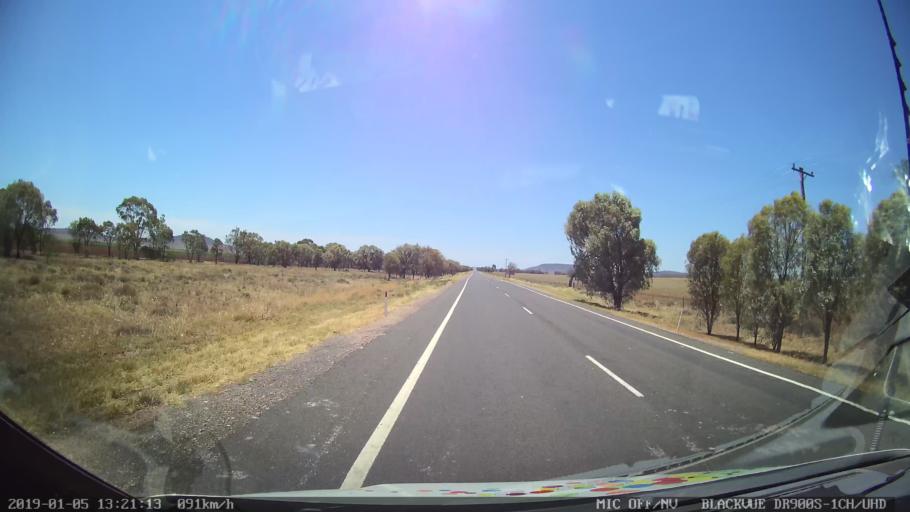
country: AU
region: New South Wales
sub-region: Gunnedah
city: Gunnedah
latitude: -31.0961
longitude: 149.9459
